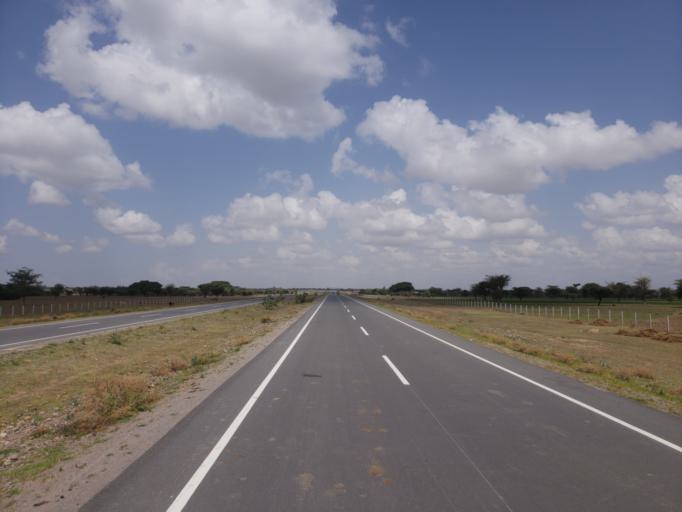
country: ET
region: Oromiya
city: Mojo
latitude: 8.2974
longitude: 38.9309
